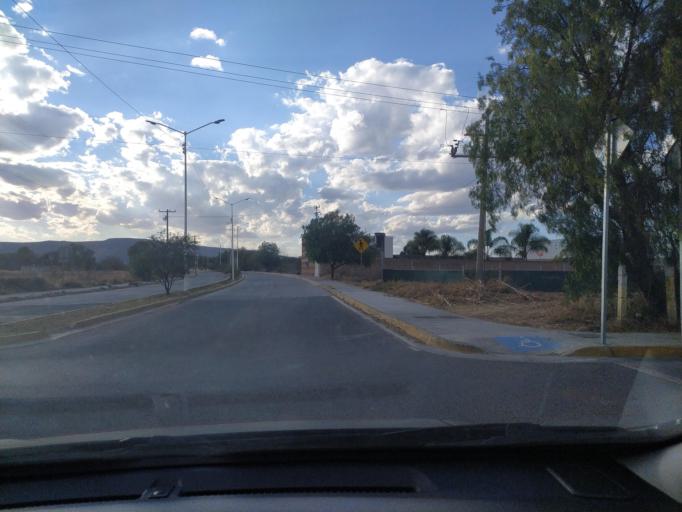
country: LA
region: Oudomxai
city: Muang La
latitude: 21.0179
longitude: 101.8341
